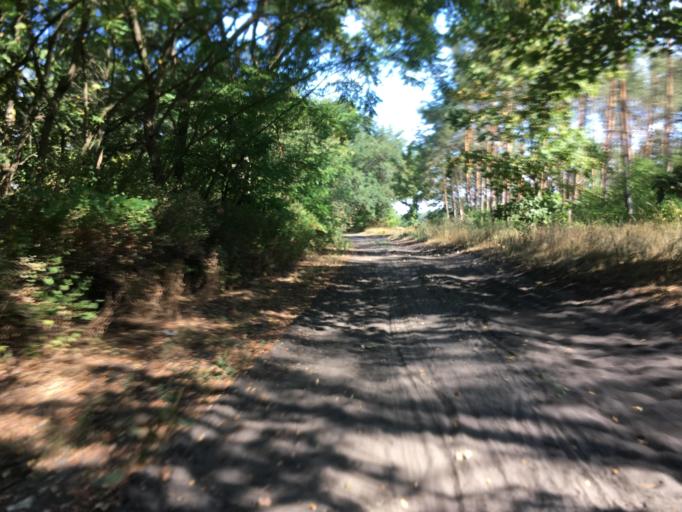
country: DE
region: Brandenburg
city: Zehdenick
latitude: 52.9665
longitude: 13.3839
